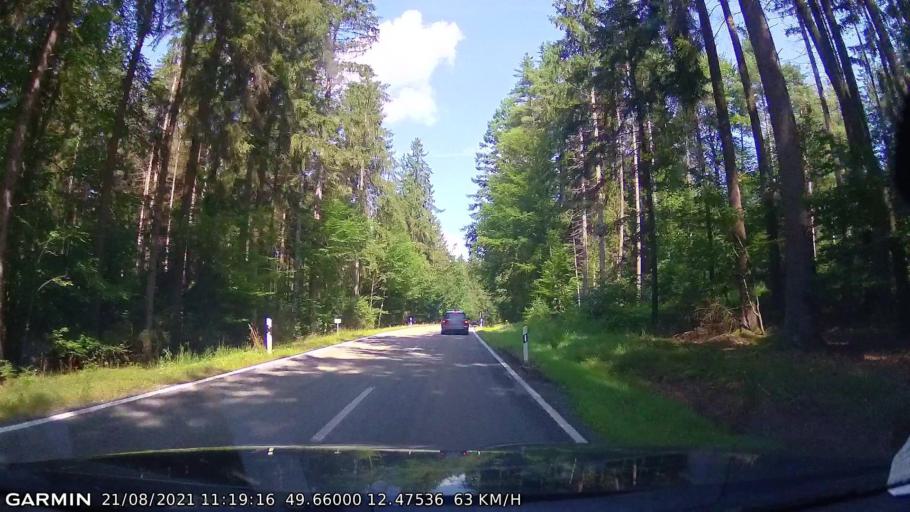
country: DE
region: Bavaria
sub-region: Upper Palatinate
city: Waidhaus
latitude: 49.6601
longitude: 12.4752
